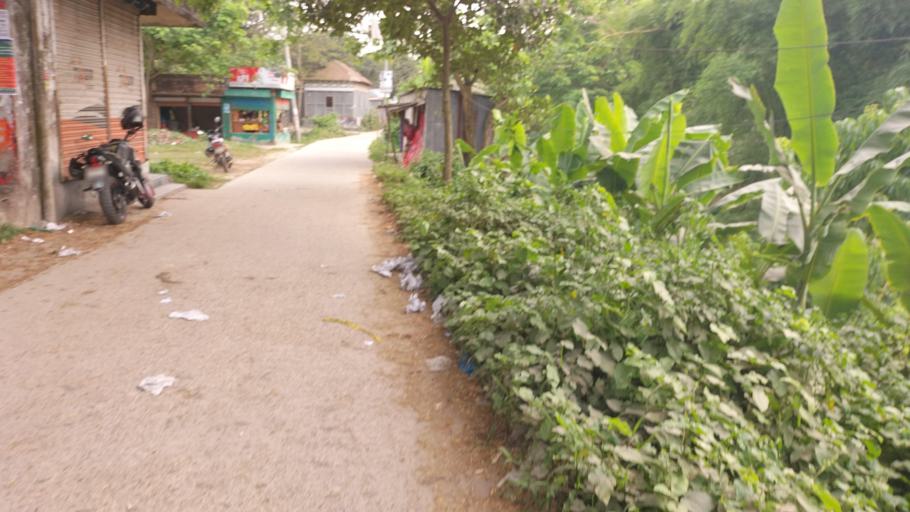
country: BD
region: Dhaka
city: Azimpur
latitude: 23.6664
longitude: 90.3410
